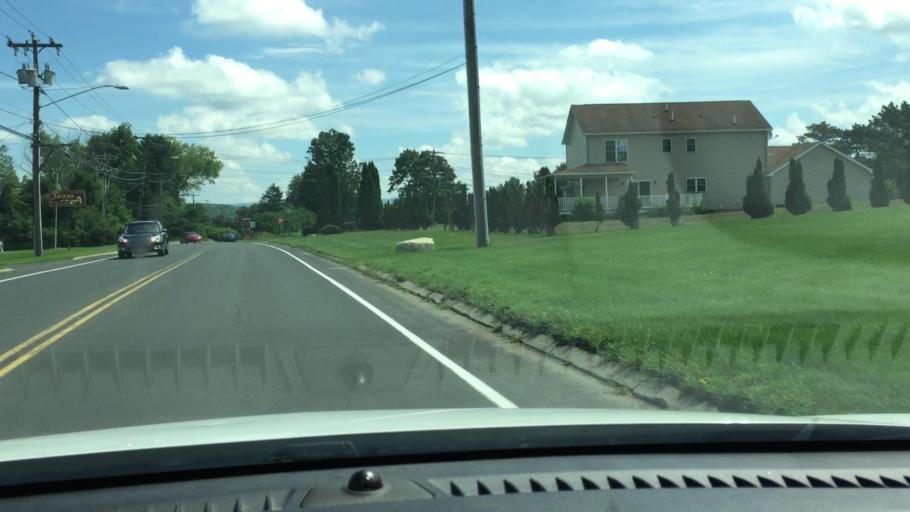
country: US
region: Massachusetts
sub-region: Berkshire County
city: Pittsfield
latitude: 42.4751
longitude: -73.2311
